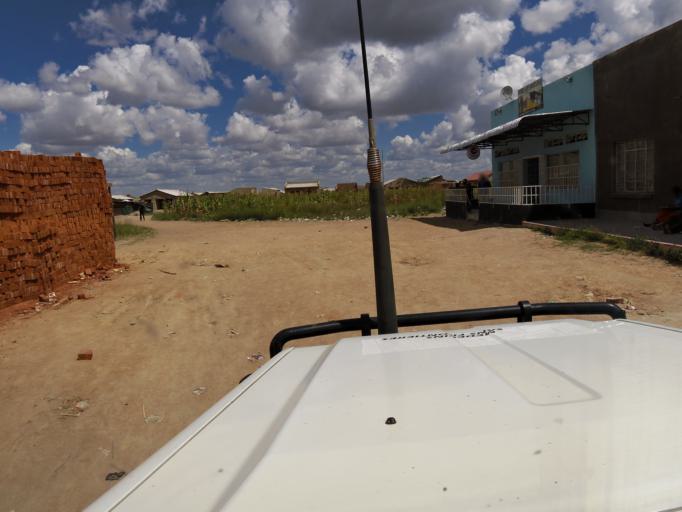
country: ZW
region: Harare
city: Epworth
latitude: -17.9232
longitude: 31.1427
